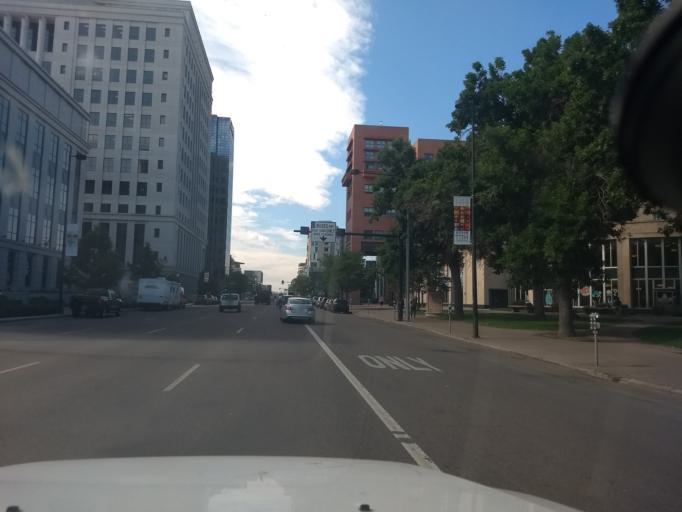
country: US
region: Colorado
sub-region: Denver County
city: Denver
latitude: 39.7383
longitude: -104.9874
